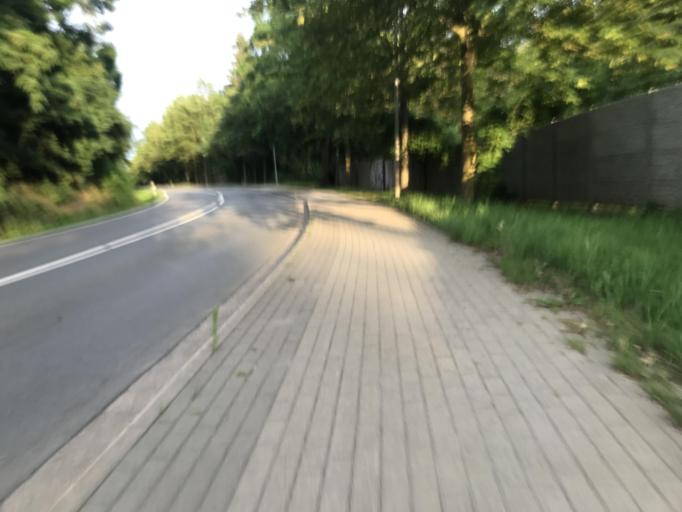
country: DE
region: Saxony-Anhalt
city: Quedlinburg
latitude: 51.8003
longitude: 11.1320
